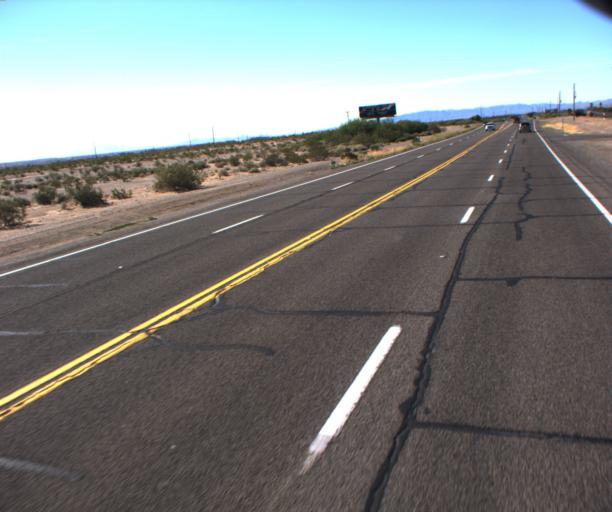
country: US
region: Arizona
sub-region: Mohave County
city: Mohave Valley
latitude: 34.9750
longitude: -114.5980
